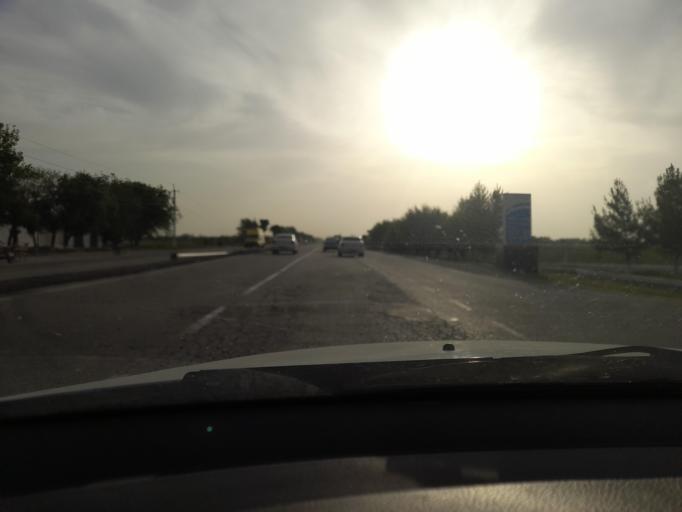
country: UZ
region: Navoiy
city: Beshrabot
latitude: 40.1382
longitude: 65.2766
